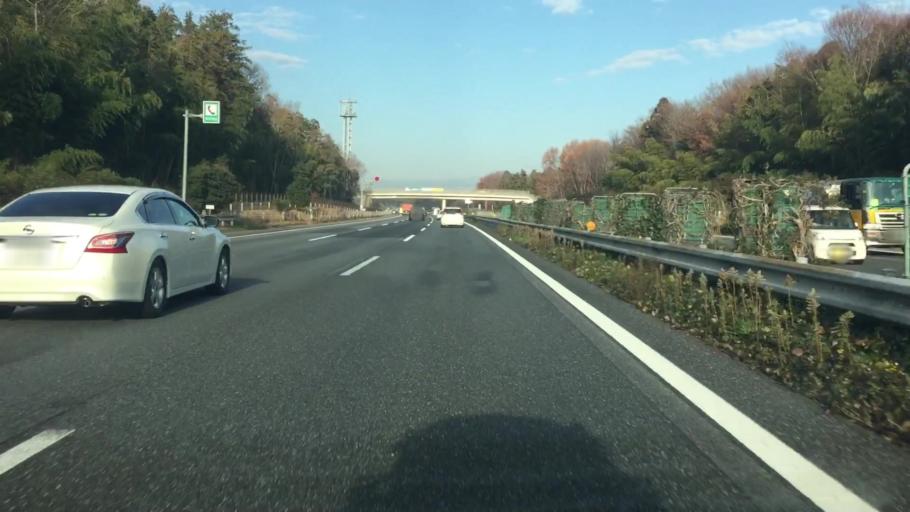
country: JP
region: Saitama
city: Ogawa
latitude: 36.1086
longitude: 139.2740
